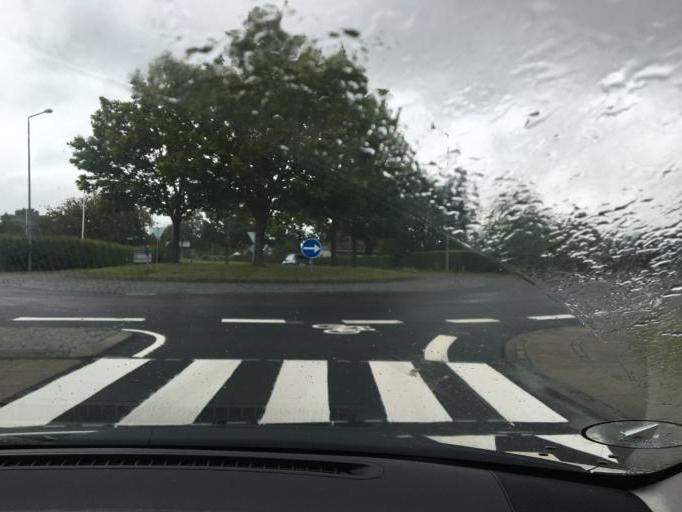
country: DK
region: South Denmark
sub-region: Middelfart Kommune
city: Middelfart
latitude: 55.4911
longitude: 9.7634
